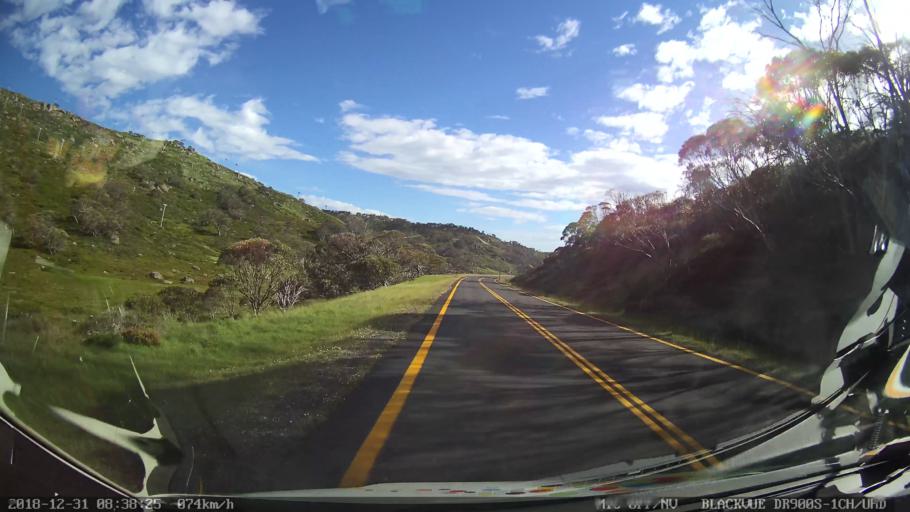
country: AU
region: New South Wales
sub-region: Snowy River
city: Jindabyne
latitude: -36.4148
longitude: 148.3954
